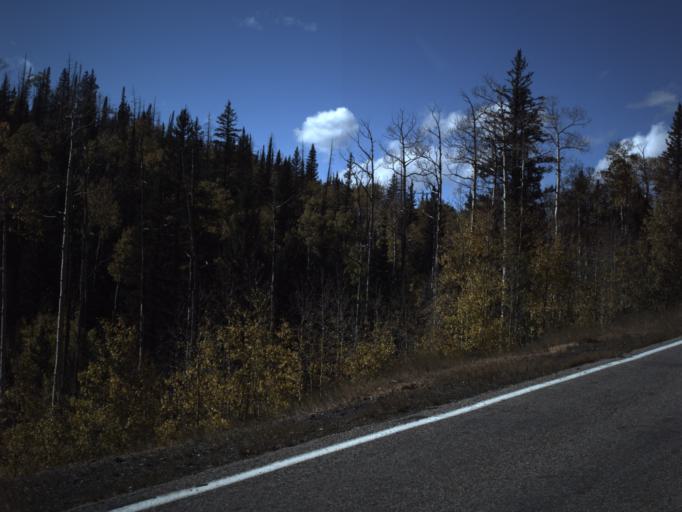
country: US
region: Utah
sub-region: Iron County
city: Parowan
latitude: 37.6618
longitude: -112.7170
